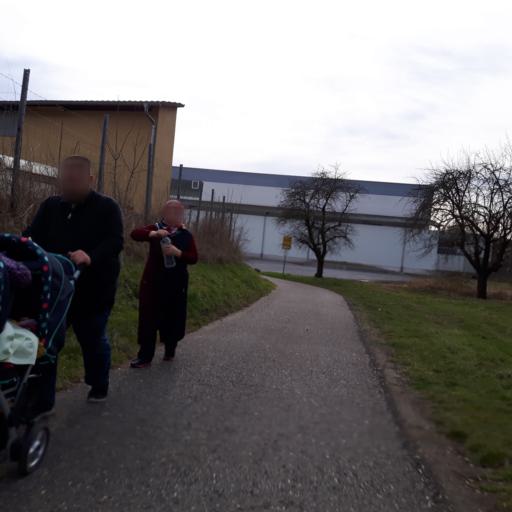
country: DE
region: Baden-Wuerttemberg
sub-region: Regierungsbezirk Stuttgart
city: Grossbottwar
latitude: 49.0004
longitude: 9.2968
